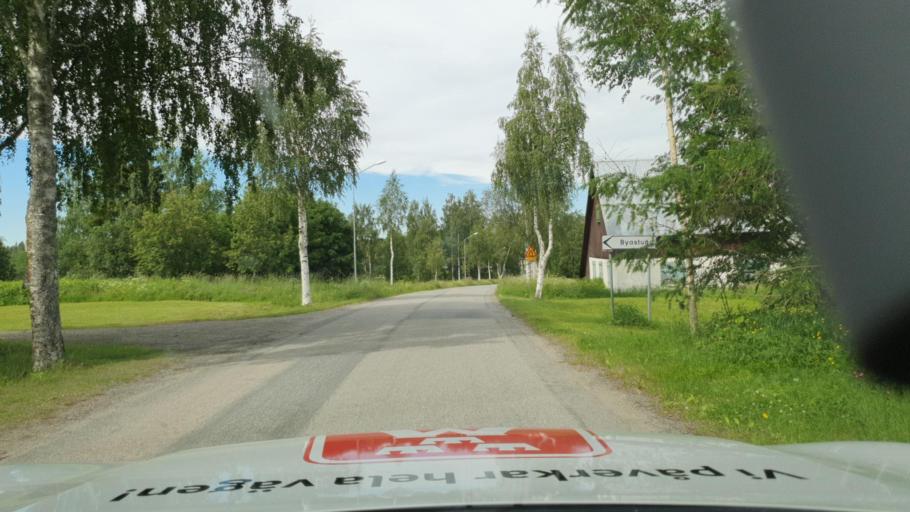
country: SE
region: Vaesterbotten
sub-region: Skelleftea Kommun
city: Burtraesk
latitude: 64.4509
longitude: 20.4818
